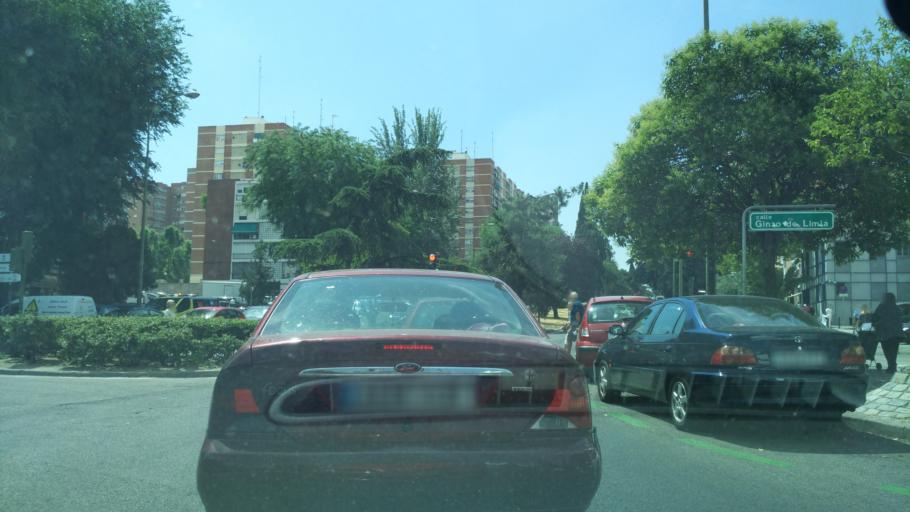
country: ES
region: Madrid
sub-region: Provincia de Madrid
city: Tetuan de las Victorias
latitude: 40.4792
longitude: -3.7043
